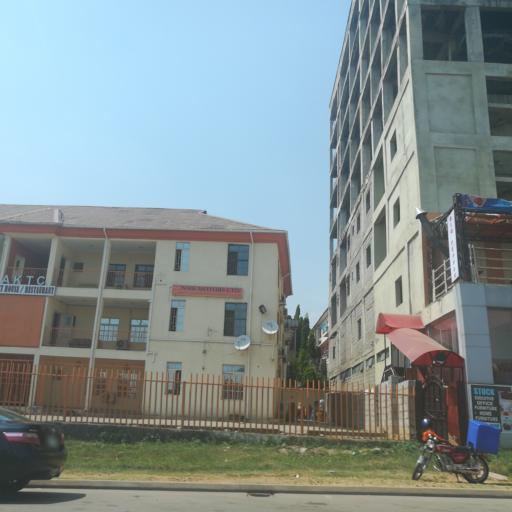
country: NG
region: Abuja Federal Capital Territory
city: Abuja
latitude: 9.0690
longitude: 7.4334
